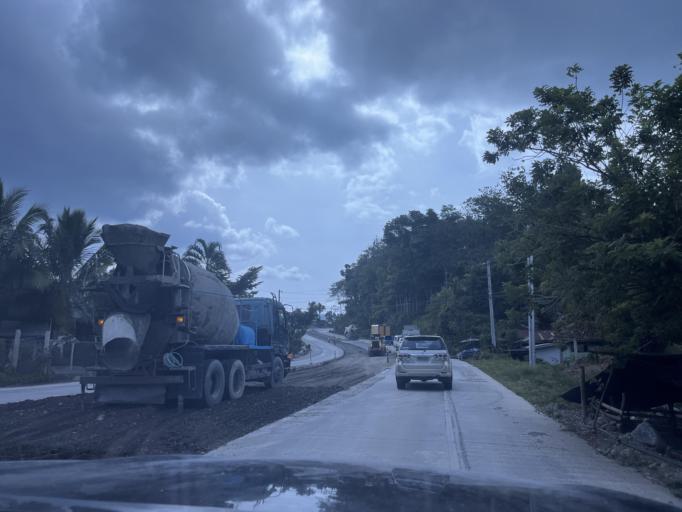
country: PH
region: Davao
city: Simod
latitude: 7.3819
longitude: 125.2769
